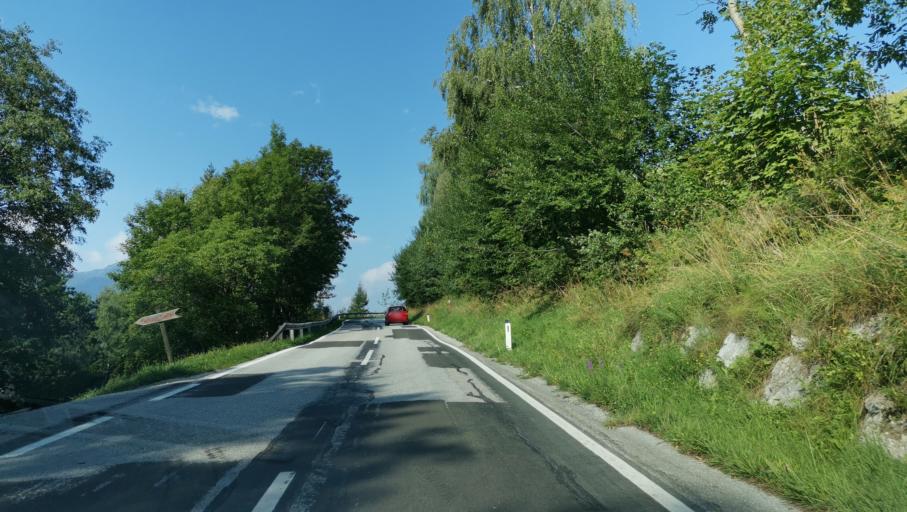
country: AT
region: Styria
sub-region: Politischer Bezirk Liezen
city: Trieben
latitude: 47.5151
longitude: 14.4525
